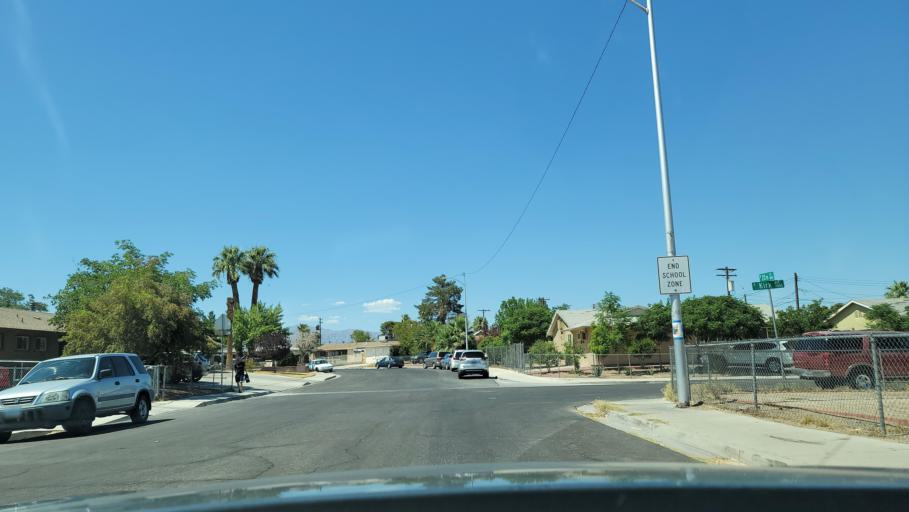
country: US
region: Nevada
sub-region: Clark County
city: Las Vegas
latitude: 36.1777
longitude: -115.1216
